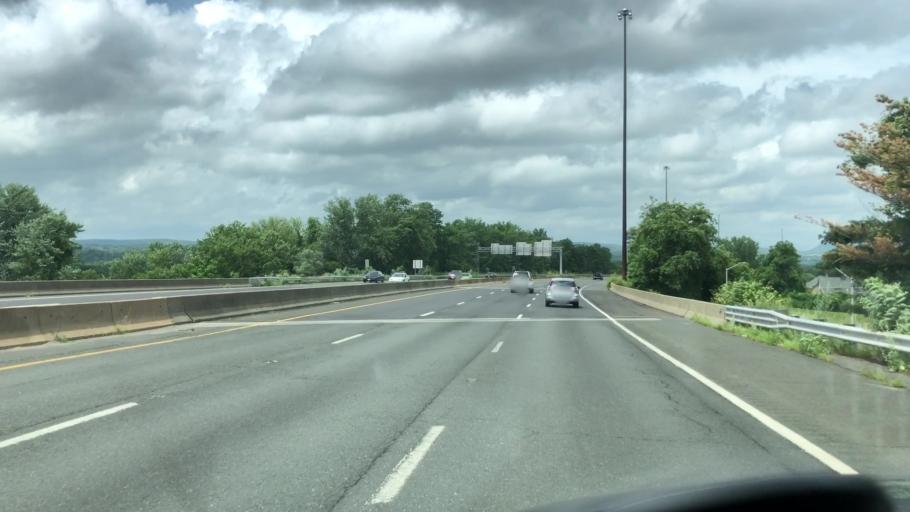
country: US
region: Massachusetts
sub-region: Hampden County
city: Chicopee
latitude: 42.1405
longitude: -72.6122
